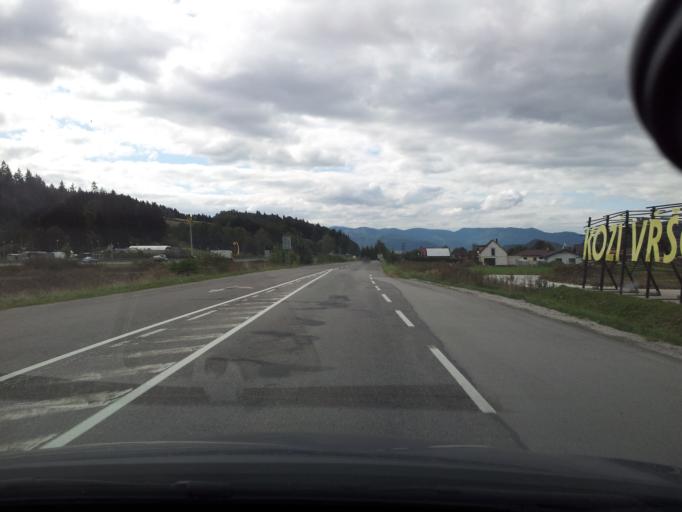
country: SK
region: Zilinsky
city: Ruzomberok
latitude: 49.0933
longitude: 19.4199
